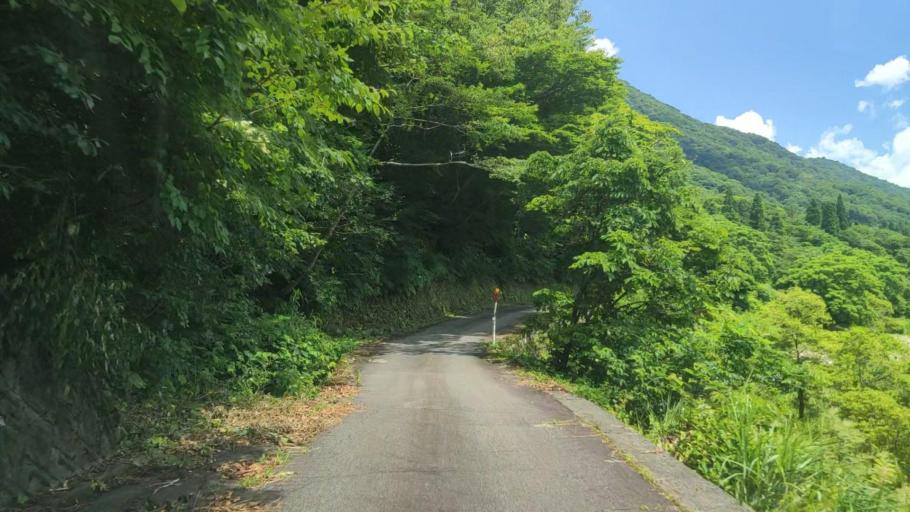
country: JP
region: Fukui
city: Ono
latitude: 35.7961
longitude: 136.4950
